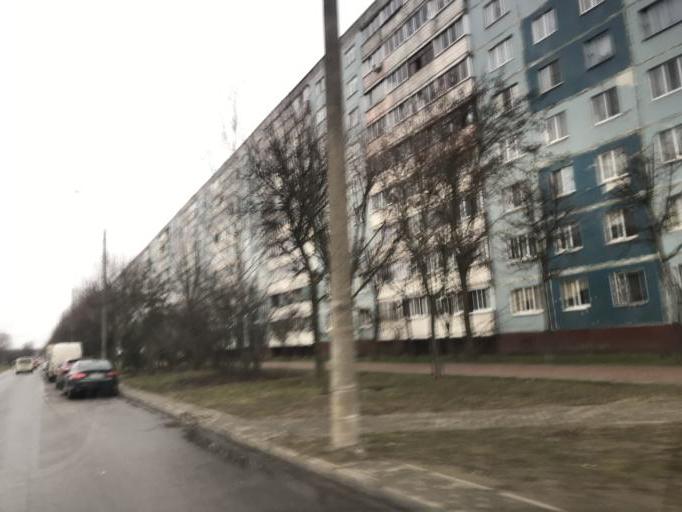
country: BY
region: Mogilev
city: Mahilyow
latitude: 53.8714
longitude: 30.3370
